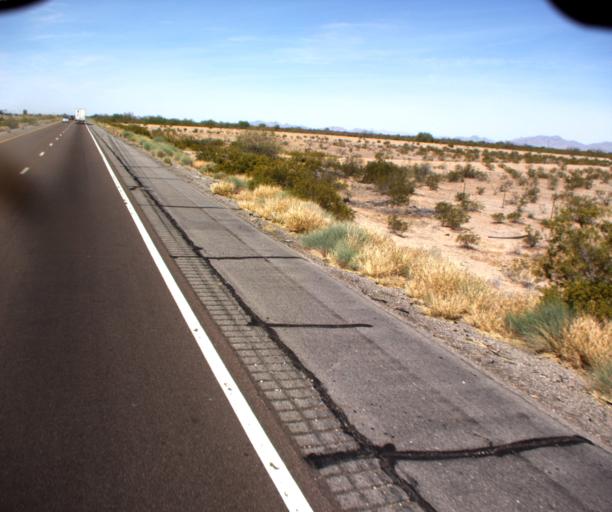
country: US
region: Arizona
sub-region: La Paz County
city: Salome
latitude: 33.5570
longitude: -113.2719
